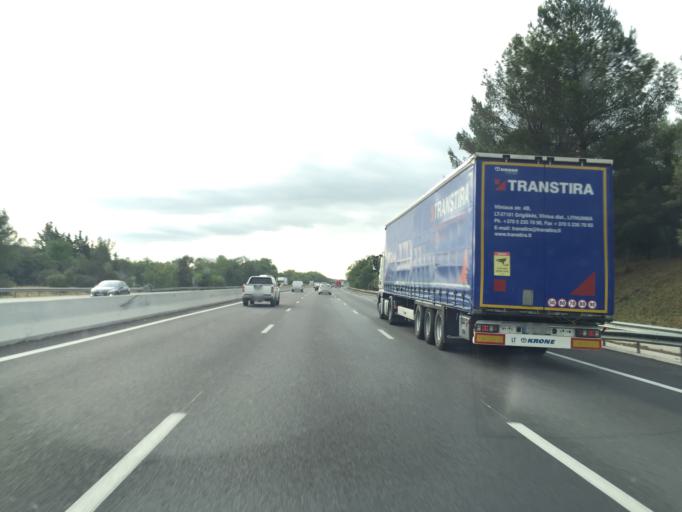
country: FR
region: Provence-Alpes-Cote d'Azur
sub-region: Departement du Var
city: Le Muy
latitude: 43.4639
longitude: 6.5780
